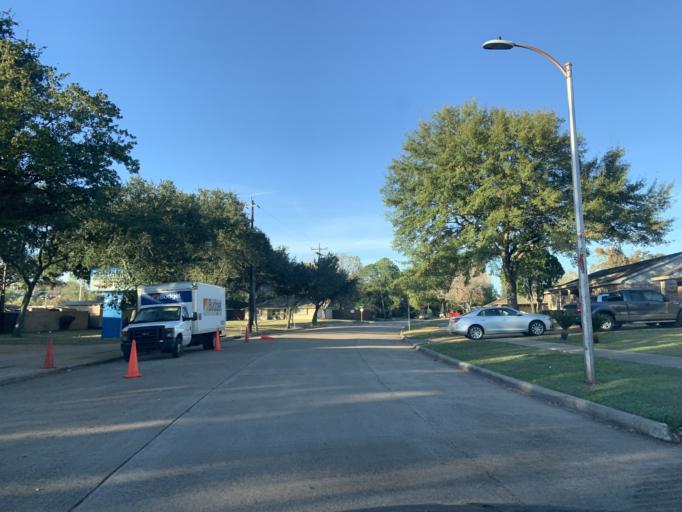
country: US
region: Texas
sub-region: Harris County
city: Bellaire
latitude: 29.6878
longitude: -95.5187
